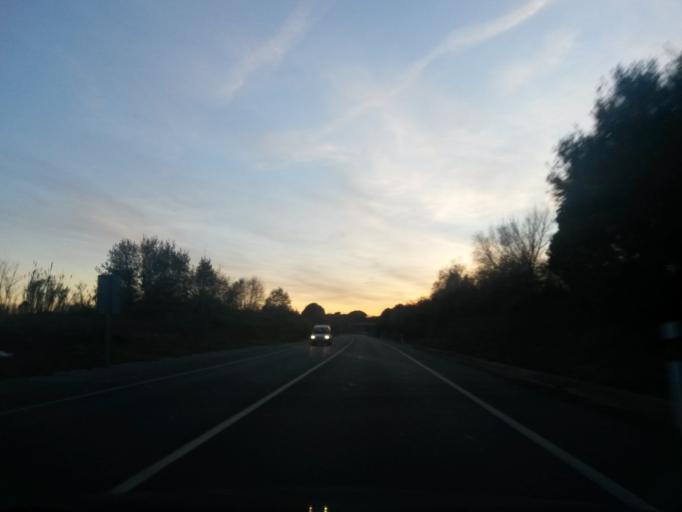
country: ES
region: Catalonia
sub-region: Provincia de Girona
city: Fornells de la Selva
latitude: 41.9331
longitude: 2.8038
